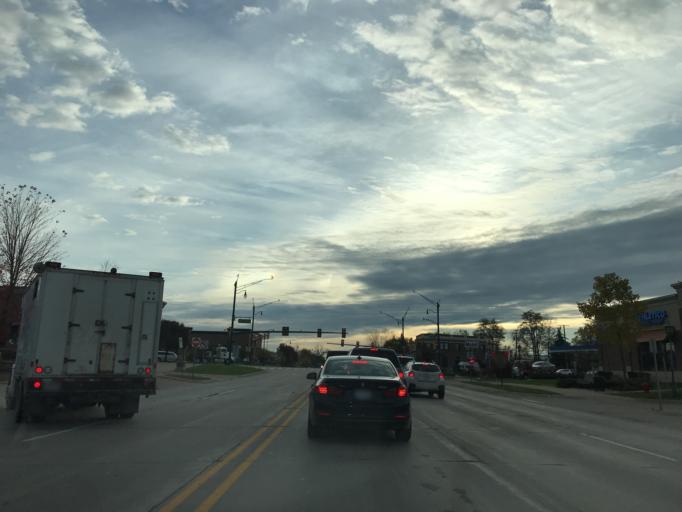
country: US
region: Michigan
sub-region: Oakland County
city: Novi
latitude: 42.4811
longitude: -83.4770
